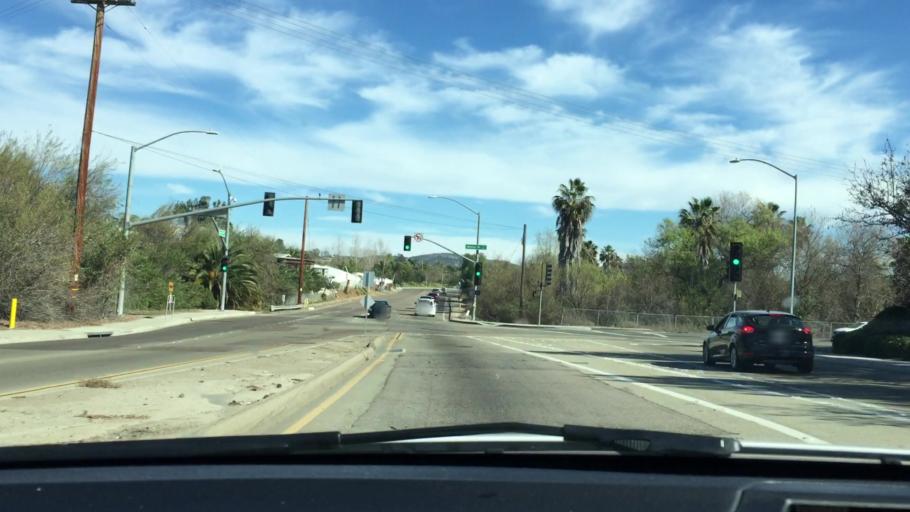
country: US
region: California
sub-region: San Diego County
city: Vista
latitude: 33.2359
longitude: -117.2622
